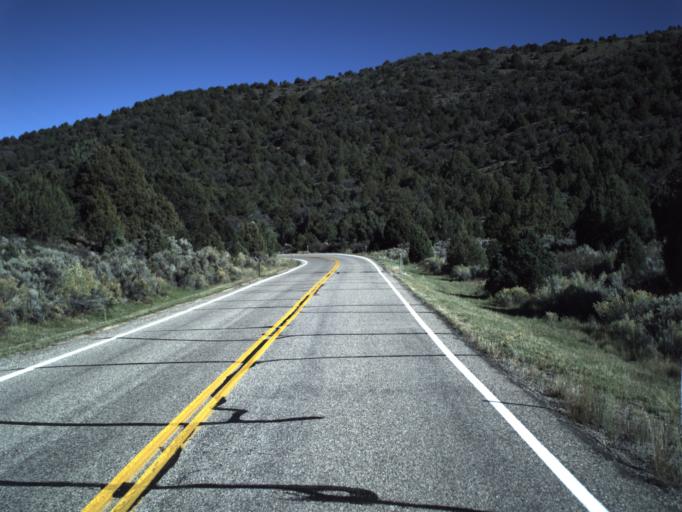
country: US
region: Utah
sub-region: Garfield County
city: Panguitch
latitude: 37.7613
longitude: -112.5090
